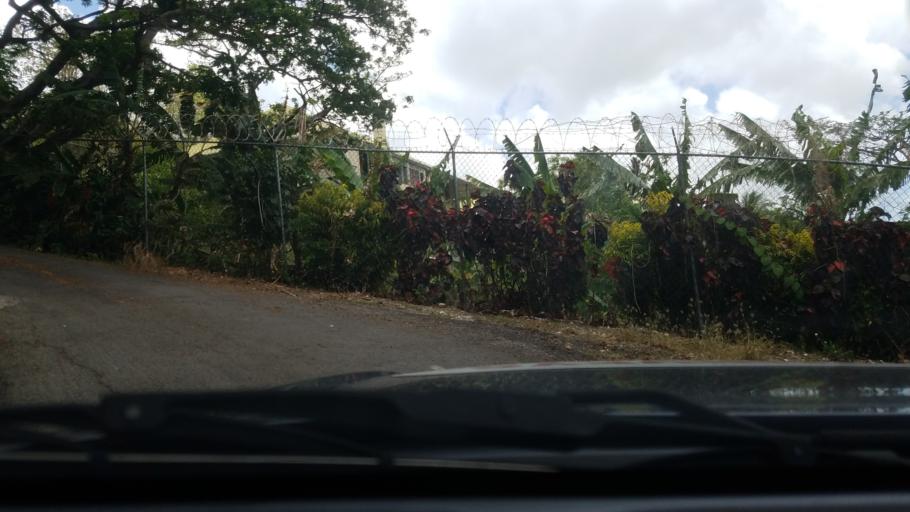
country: LC
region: Castries Quarter
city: Castries
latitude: 14.0190
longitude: -60.9989
